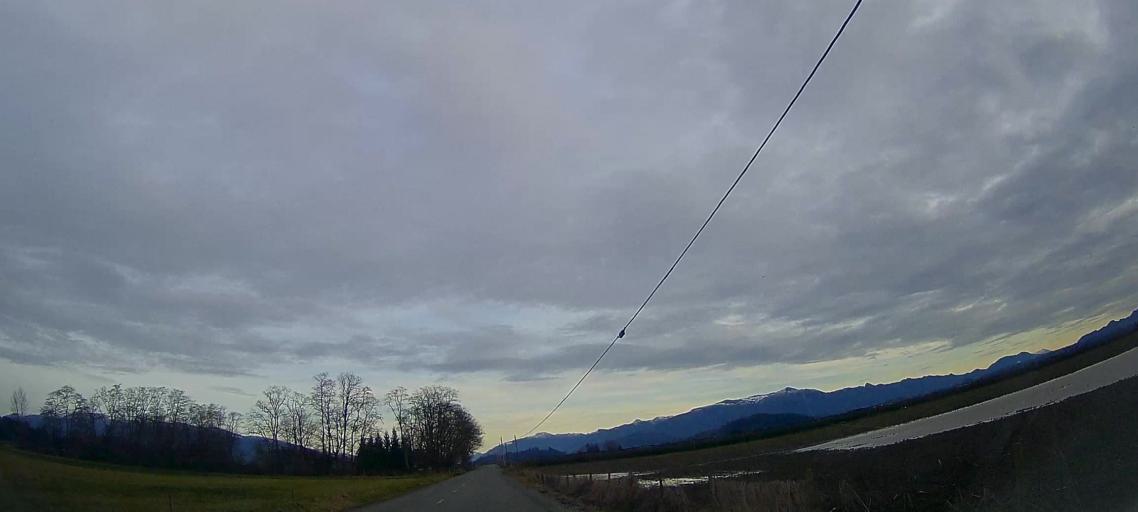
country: US
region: Washington
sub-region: Skagit County
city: Burlington
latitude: 48.5013
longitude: -122.3910
